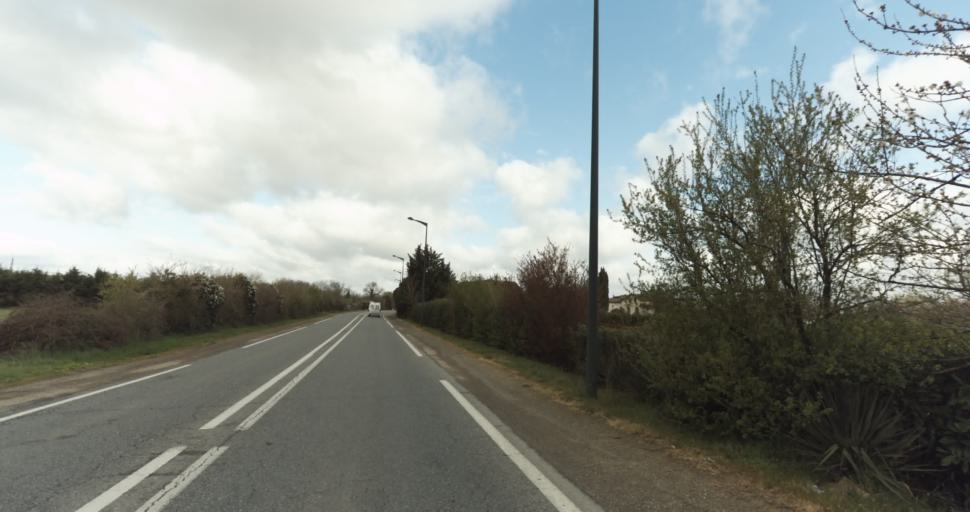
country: FR
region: Midi-Pyrenees
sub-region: Departement de la Haute-Garonne
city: Miremont
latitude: 43.3706
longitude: 1.4487
